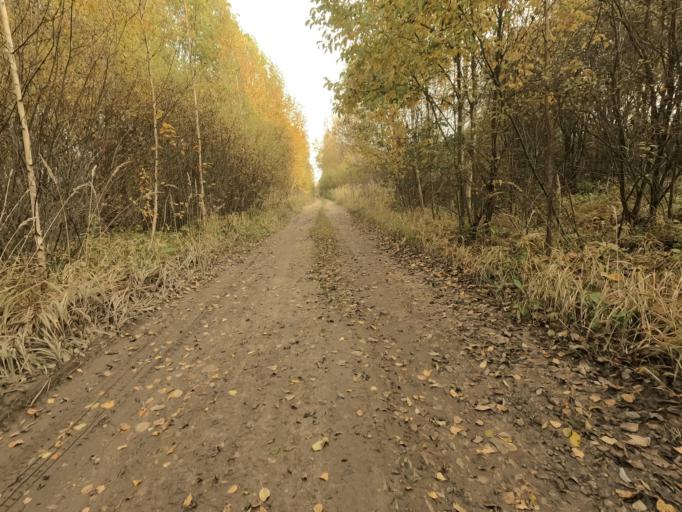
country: RU
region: Novgorod
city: Batetskiy
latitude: 58.8797
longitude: 30.7998
